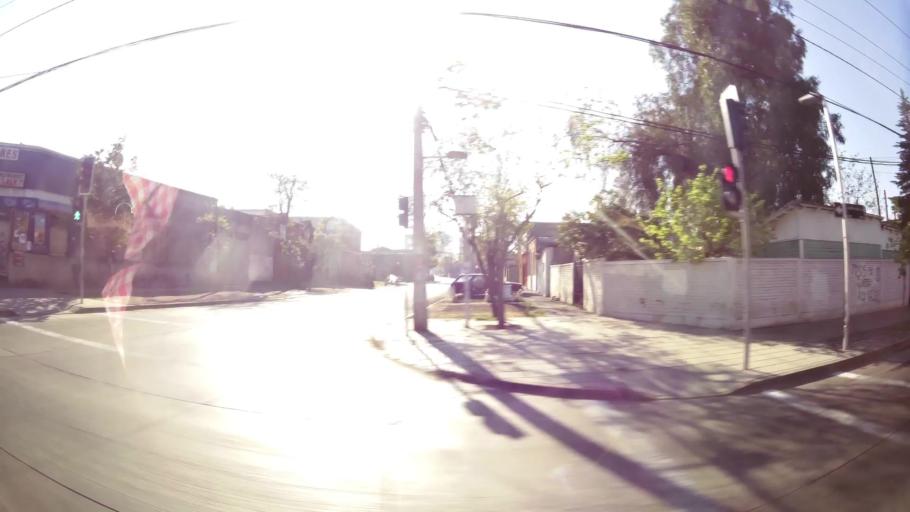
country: CL
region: Santiago Metropolitan
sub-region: Provincia de Santiago
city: Santiago
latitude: -33.4711
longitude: -70.6332
